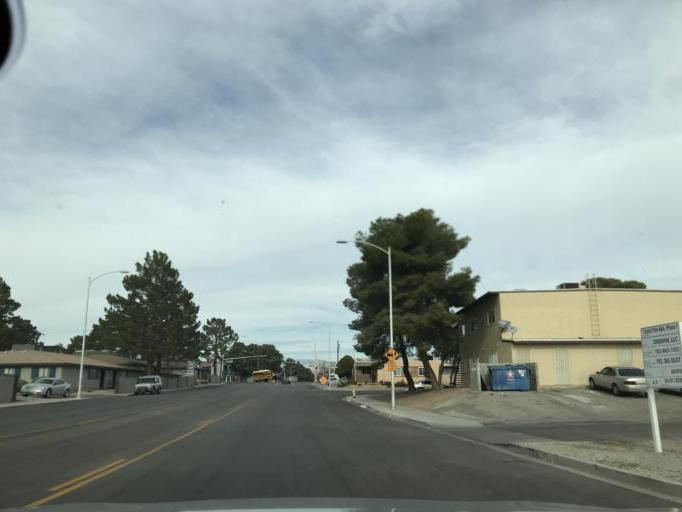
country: US
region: Nevada
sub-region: Clark County
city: Las Vegas
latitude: 36.2155
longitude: -115.2166
